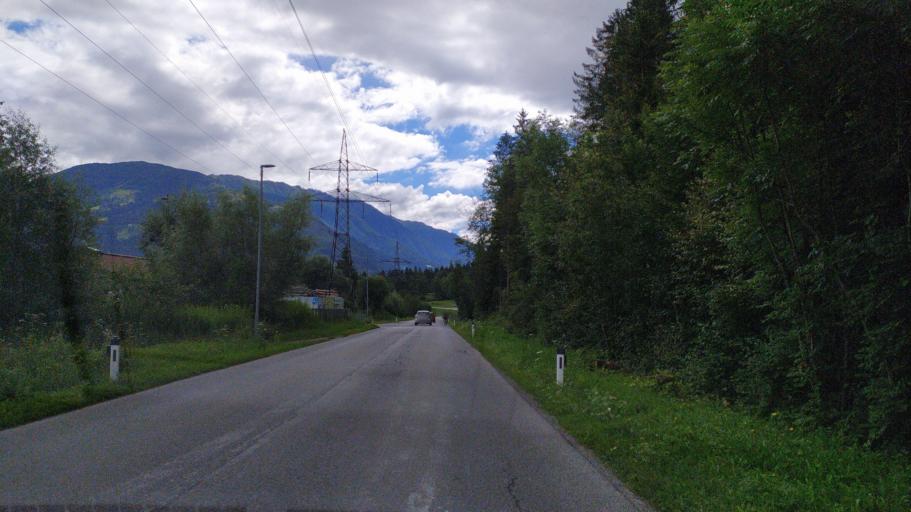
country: AT
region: Tyrol
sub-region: Politischer Bezirk Lienz
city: Tristach
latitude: 46.8143
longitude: 12.8050
